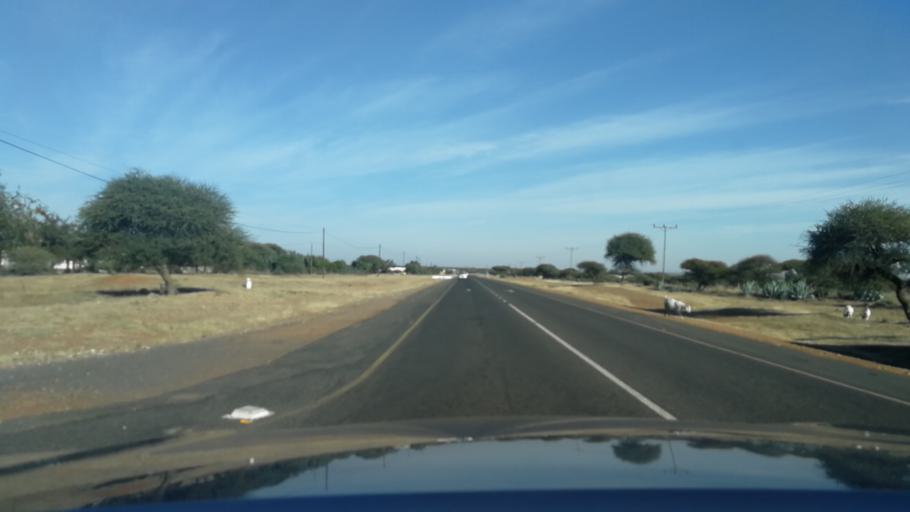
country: BW
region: South East
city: Janeng
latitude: -25.4684
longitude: 25.5708
